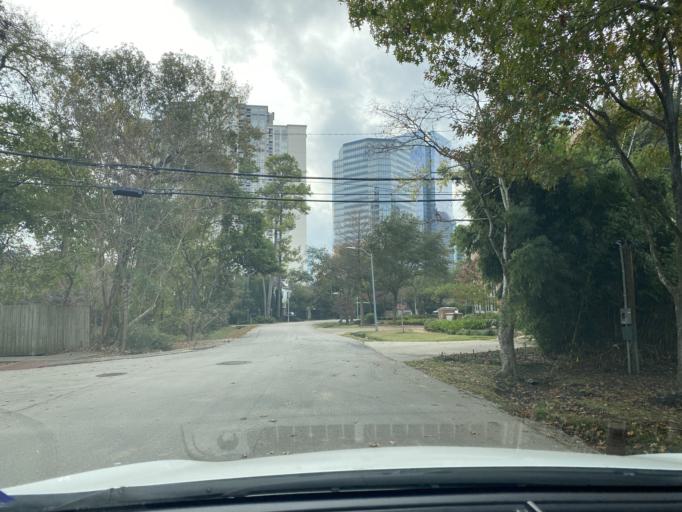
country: US
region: Texas
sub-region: Harris County
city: Hunters Creek Village
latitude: 29.7561
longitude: -95.4596
